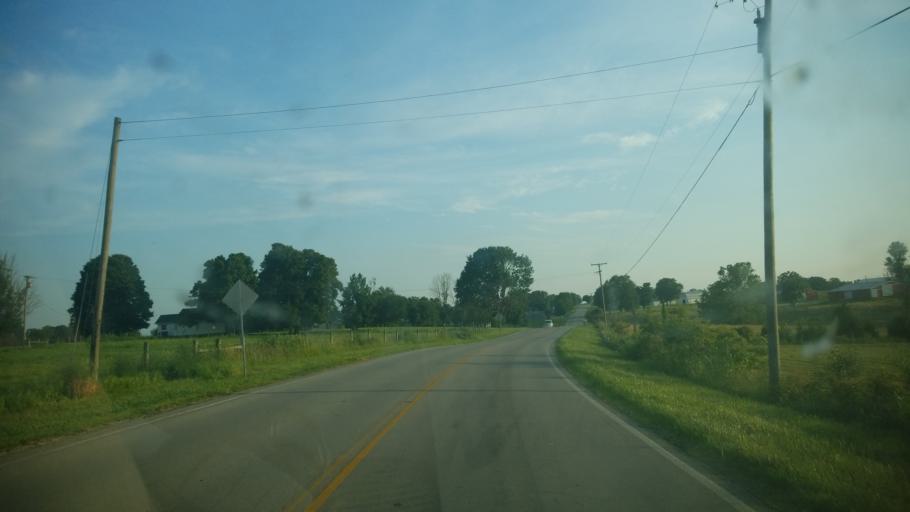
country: US
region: Ohio
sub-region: Adams County
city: Peebles
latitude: 38.9312
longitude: -83.4181
